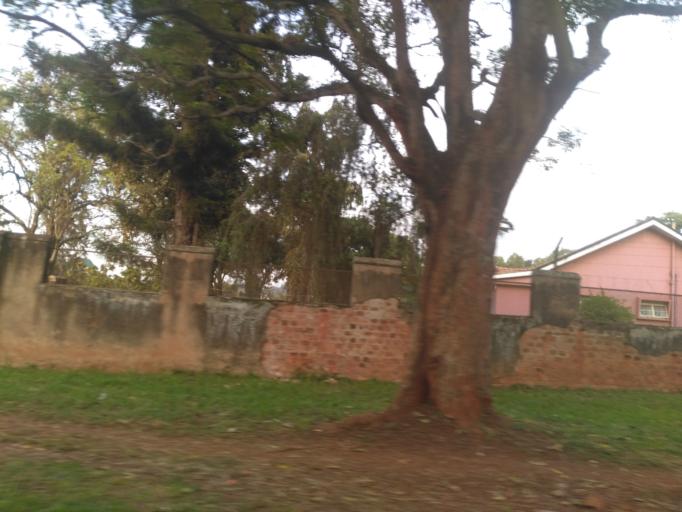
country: UG
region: Eastern Region
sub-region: Jinja District
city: Jinja
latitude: 0.4408
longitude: 33.1978
